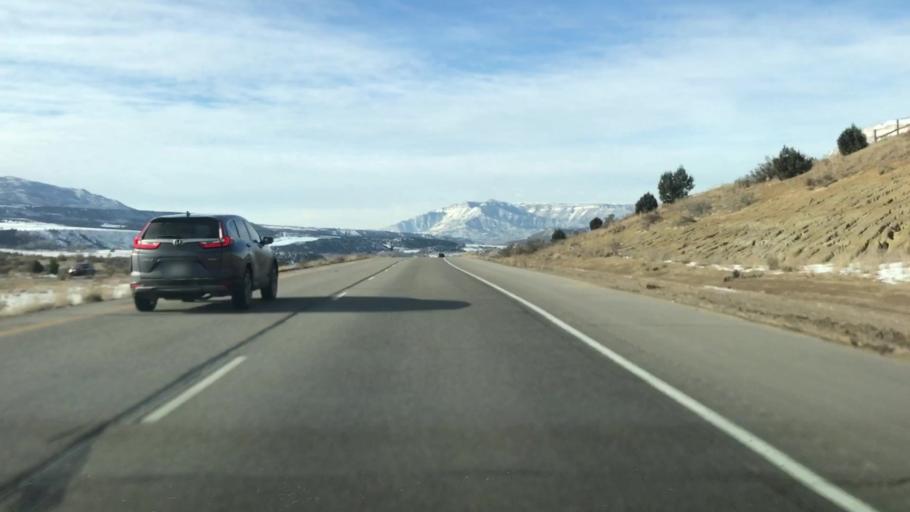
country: US
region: Colorado
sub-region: Garfield County
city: Rifle
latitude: 39.5082
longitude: -107.8818
